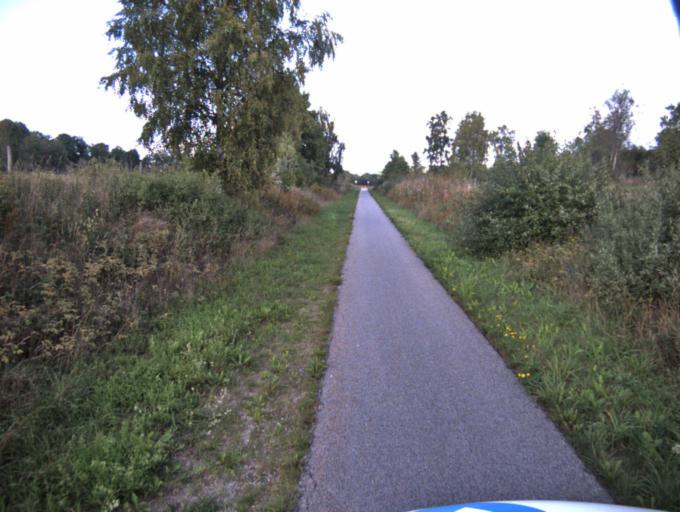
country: SE
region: Vaestra Goetaland
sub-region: Ulricehamns Kommun
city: Ulricehamn
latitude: 57.9139
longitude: 13.4805
